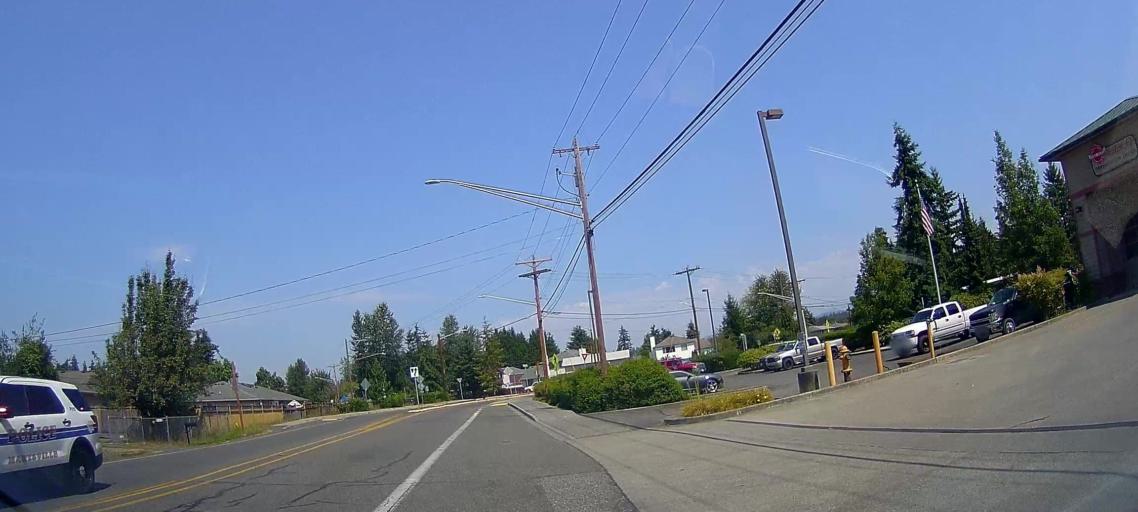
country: US
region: Washington
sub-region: Snohomish County
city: Marysville
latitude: 48.0919
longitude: -122.1629
